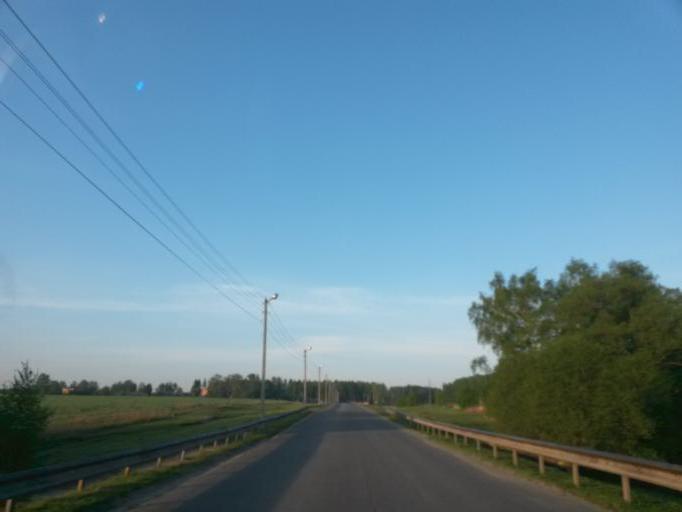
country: RU
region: Moskovskaya
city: Lyubuchany
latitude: 55.2500
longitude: 37.5336
